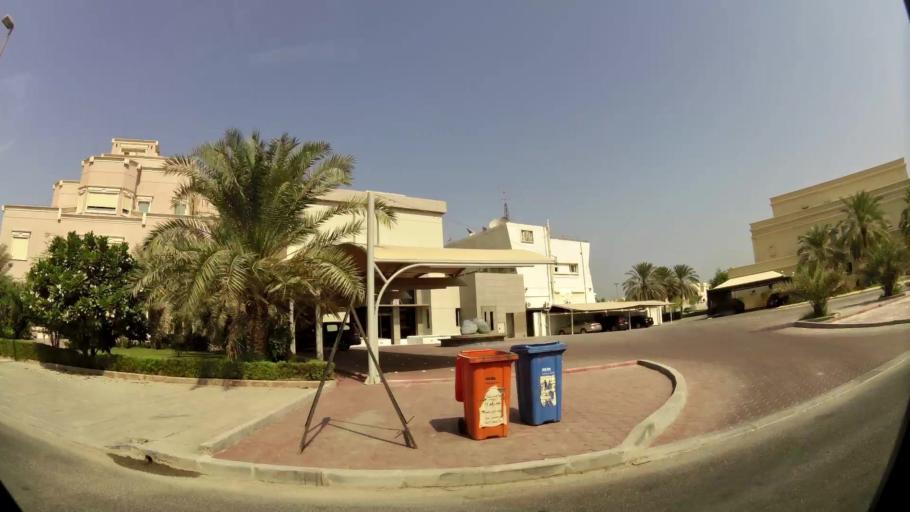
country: KW
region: Al Asimah
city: Ash Shamiyah
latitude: 29.3464
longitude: 47.9580
